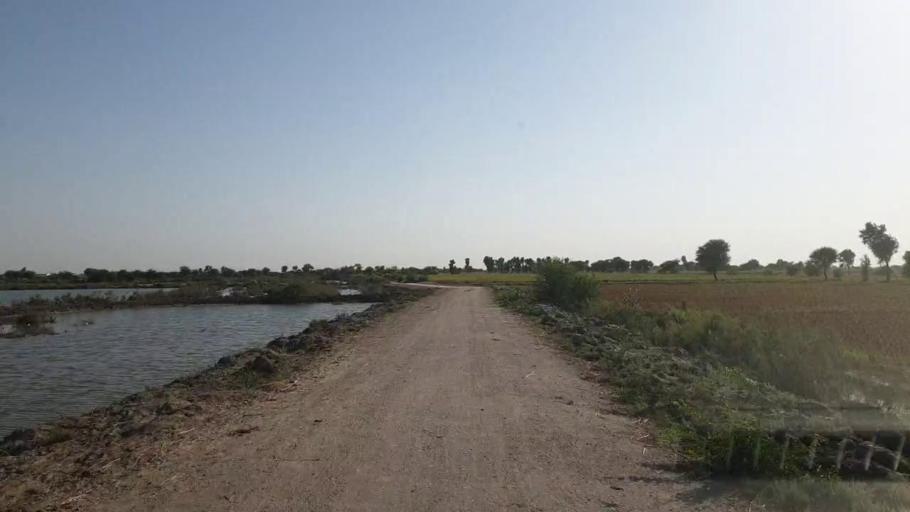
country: PK
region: Sindh
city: Badin
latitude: 24.5957
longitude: 68.9111
